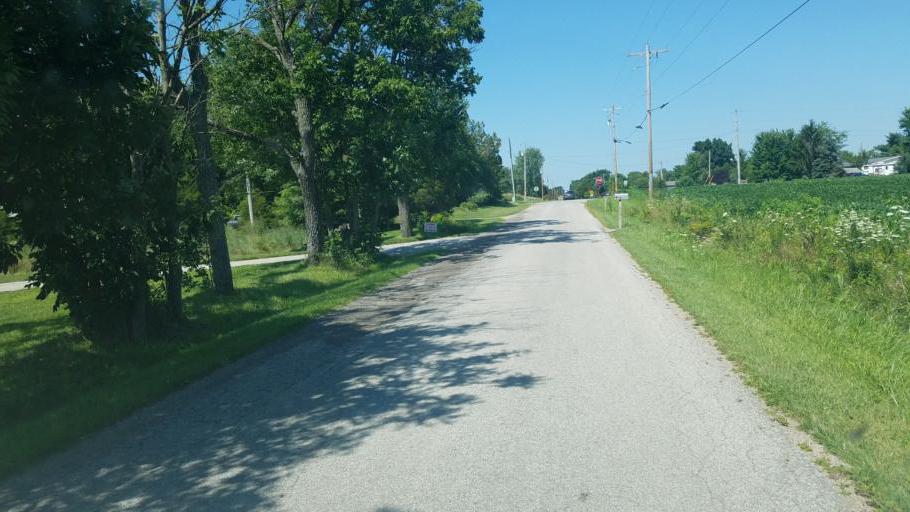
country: US
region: Ohio
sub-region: Delaware County
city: Ashley
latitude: 40.4334
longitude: -83.0097
